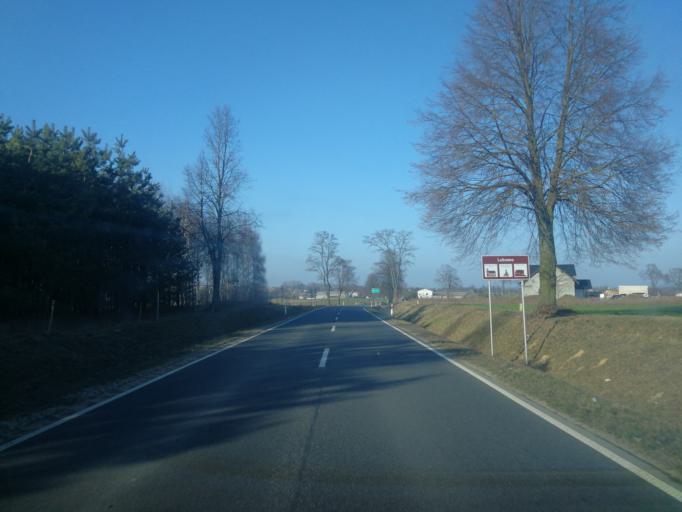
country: PL
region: Warmian-Masurian Voivodeship
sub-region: Powiat ilawski
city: Lubawa
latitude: 53.4490
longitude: 19.7774
